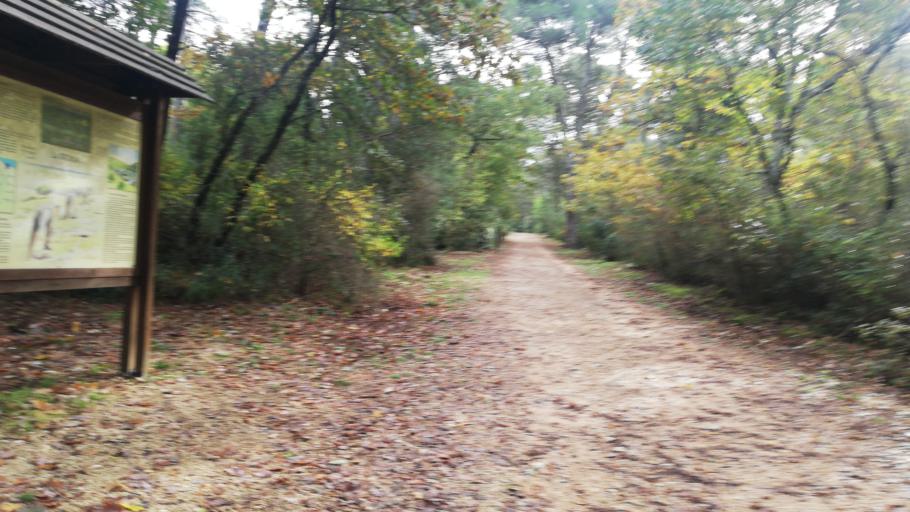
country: IT
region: Apulia
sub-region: Provincia di Bari
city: Cassano delle Murge
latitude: 40.8833
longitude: 16.7063
